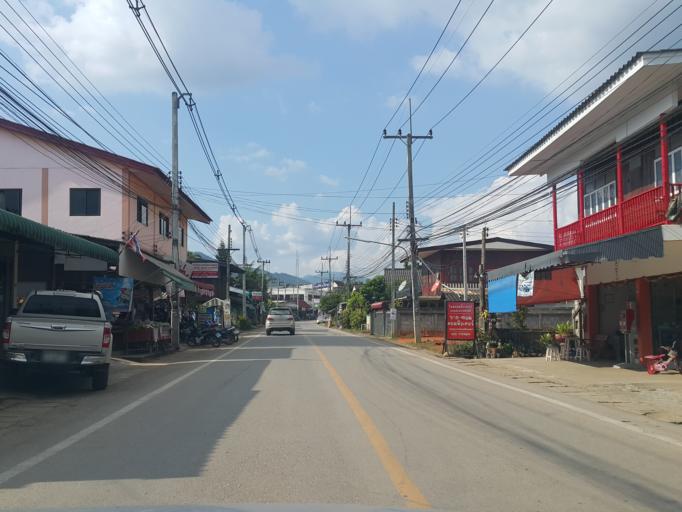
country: TH
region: Chiang Mai
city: Mae Chaem
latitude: 18.5032
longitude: 98.3609
